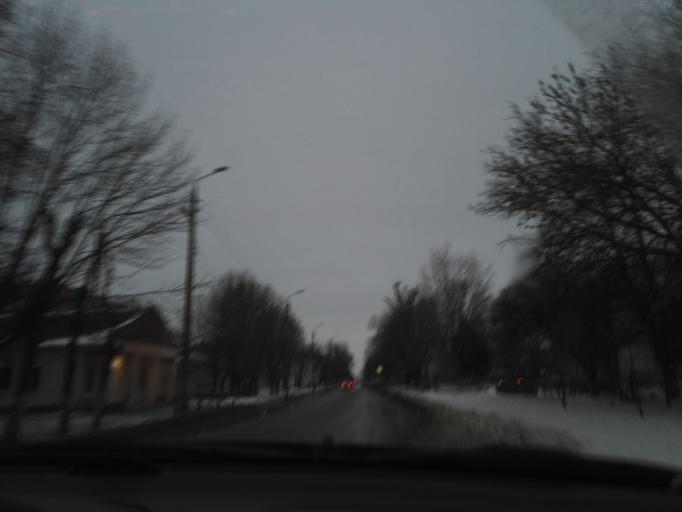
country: RU
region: Tula
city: Novomoskovsk
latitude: 54.0095
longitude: 38.3004
